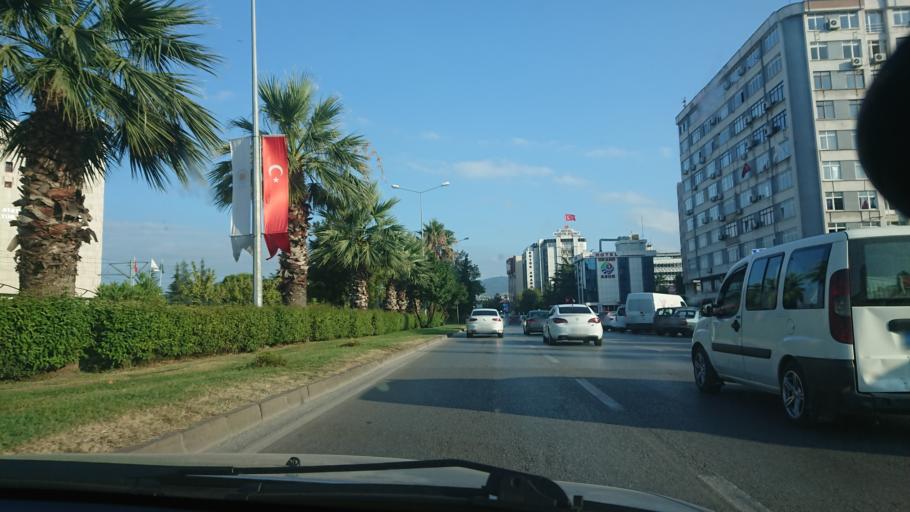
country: TR
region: Samsun
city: Samsun
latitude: 41.2947
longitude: 36.3336
